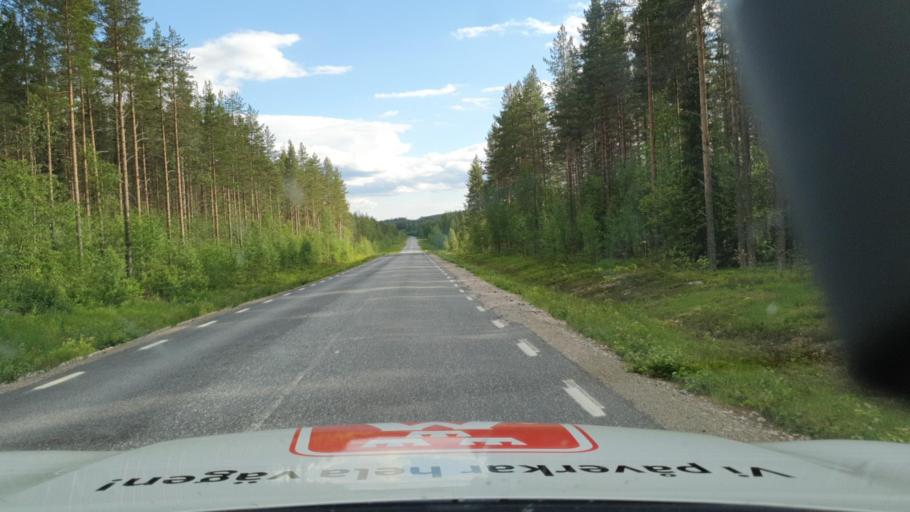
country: SE
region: Vaesterbotten
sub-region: Skelleftea Kommun
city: Langsele
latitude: 64.5876
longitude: 19.9308
